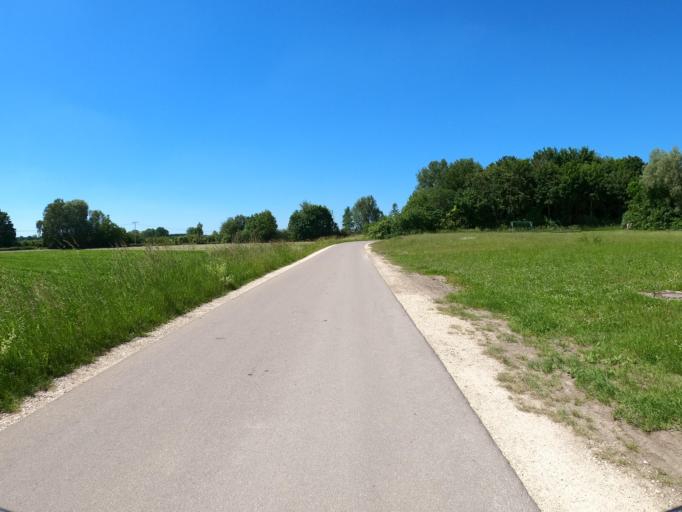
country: DE
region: Bavaria
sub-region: Swabia
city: Pfaffenhofen an der Roth
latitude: 48.3721
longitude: 10.1516
